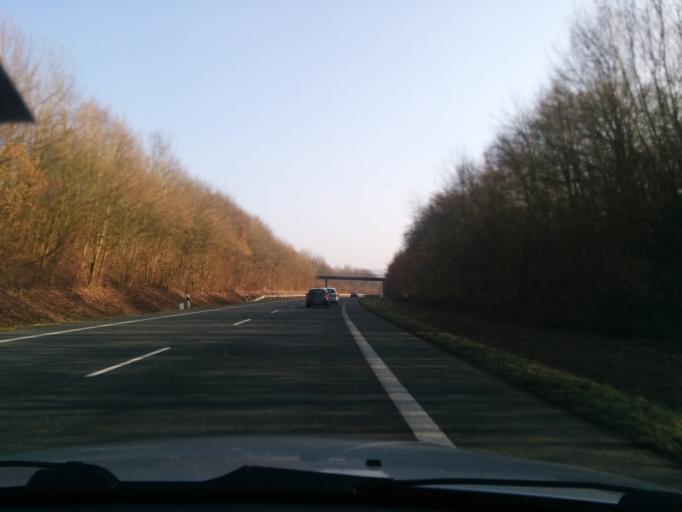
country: DE
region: North Rhine-Westphalia
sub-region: Regierungsbezirk Detmold
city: Dorentrup
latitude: 51.9787
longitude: 9.0158
